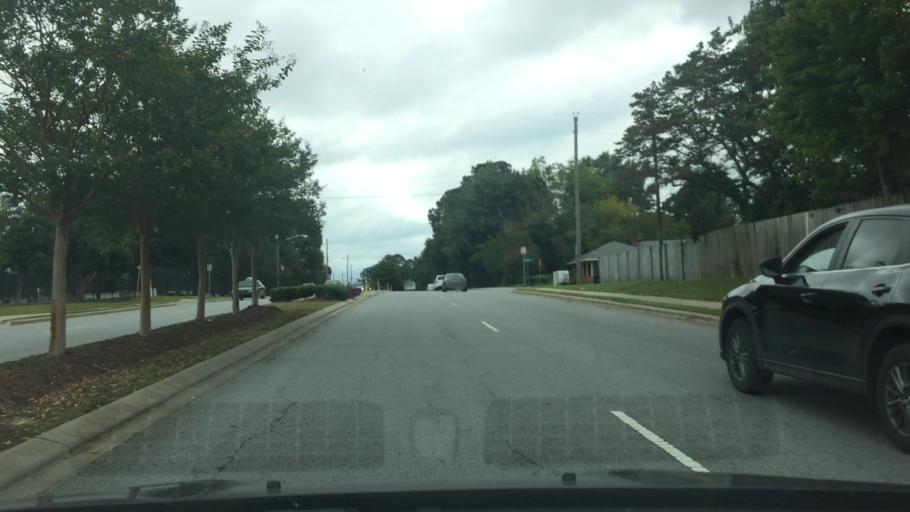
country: US
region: North Carolina
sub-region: Pitt County
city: Greenville
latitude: 35.5961
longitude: -77.3698
